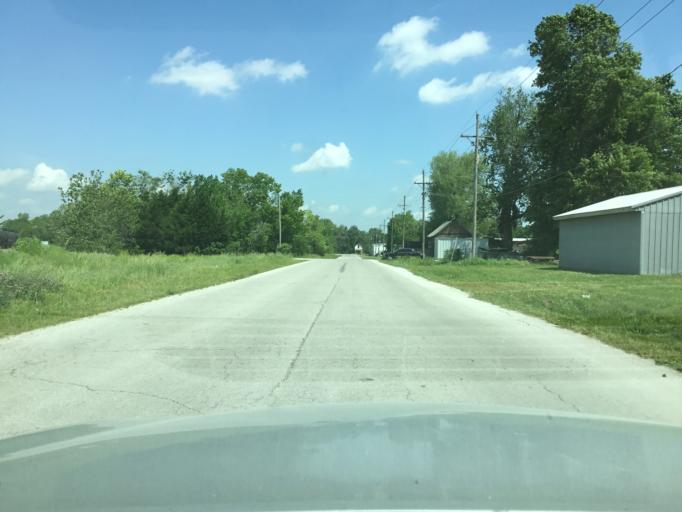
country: US
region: Kansas
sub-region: Labette County
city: Parsons
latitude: 37.3449
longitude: -95.2657
